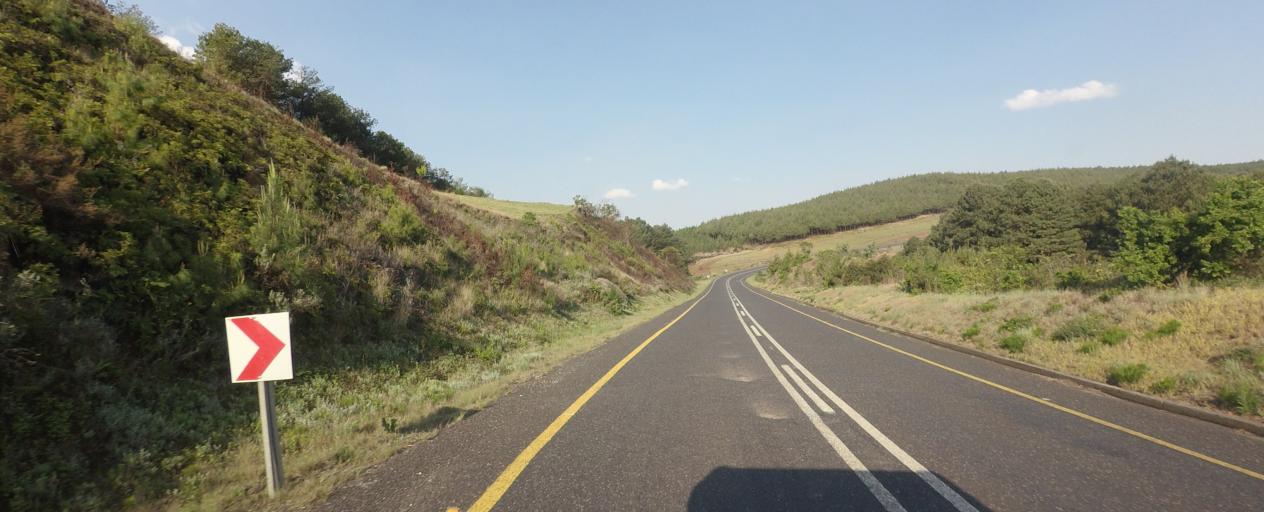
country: ZA
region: Mpumalanga
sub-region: Ehlanzeni District
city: Lydenburg
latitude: -25.1658
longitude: 30.6454
